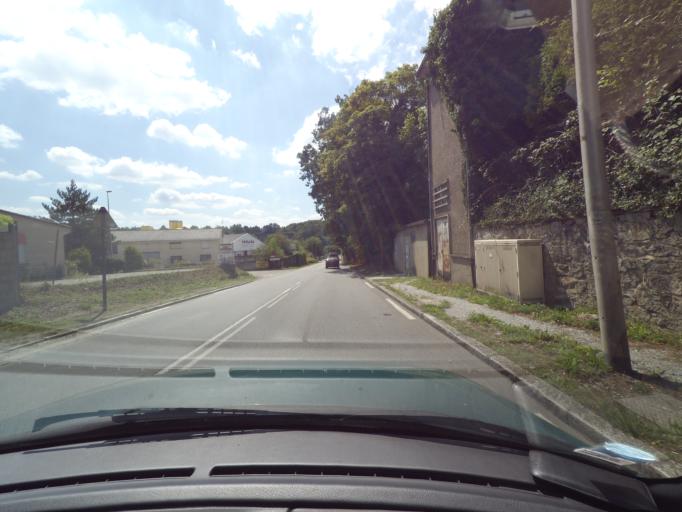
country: FR
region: Limousin
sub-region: Departement de la Haute-Vienne
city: Limoges
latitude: 45.8098
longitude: 1.2567
